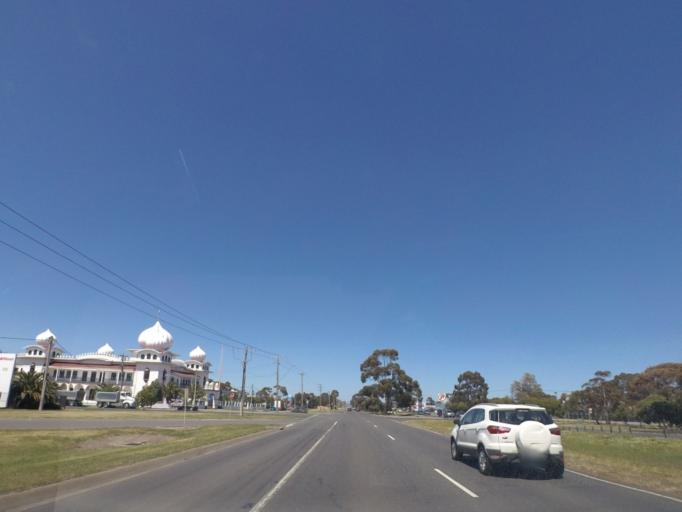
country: AU
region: Victoria
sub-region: Hume
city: Craigieburn
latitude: -37.6119
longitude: 144.9465
